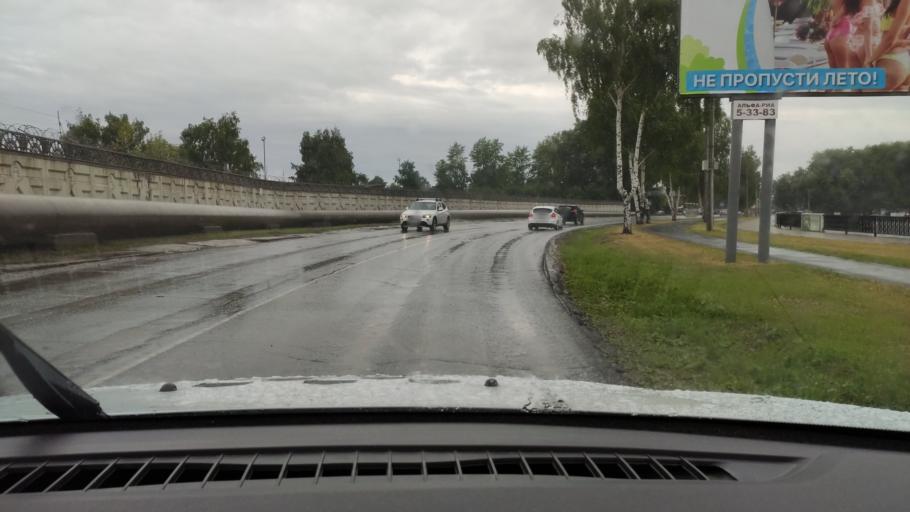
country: RU
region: Udmurtiya
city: Votkinsk
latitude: 57.0515
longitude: 53.9763
